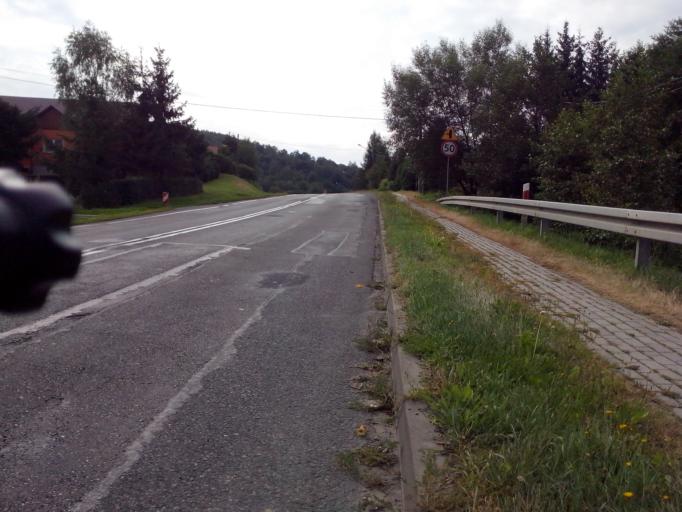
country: PL
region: Subcarpathian Voivodeship
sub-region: Powiat brzozowski
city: Domaradz
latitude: 49.7848
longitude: 21.9476
